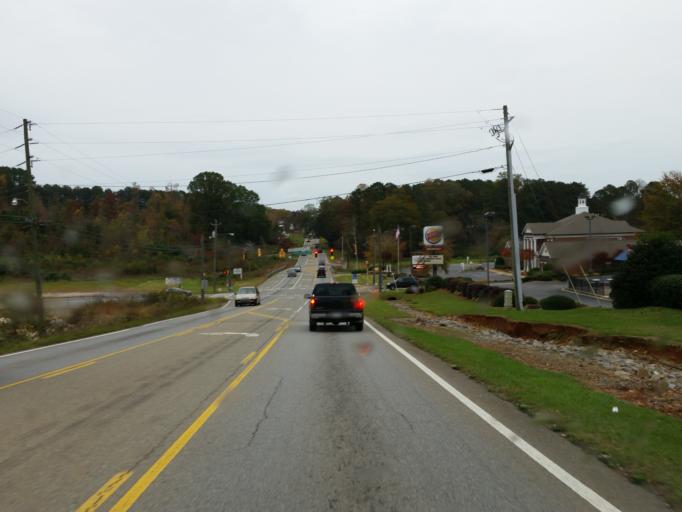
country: US
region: Georgia
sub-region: Pickens County
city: Jasper
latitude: 34.4656
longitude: -84.4517
